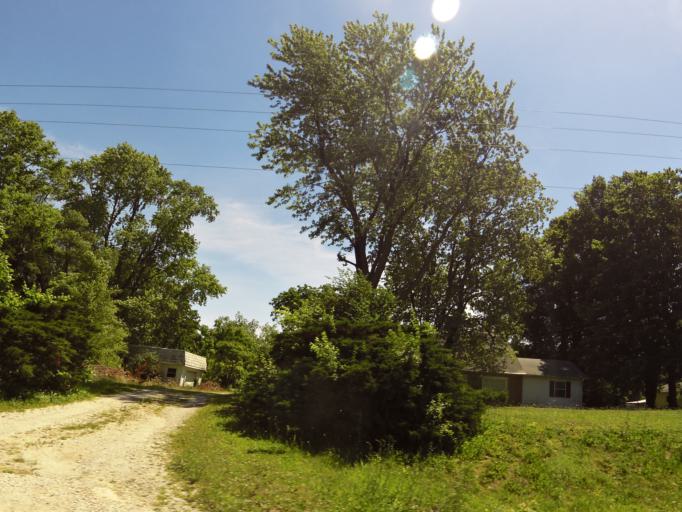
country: US
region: Illinois
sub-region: Vermilion County
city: Danville
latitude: 40.2388
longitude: -87.6442
